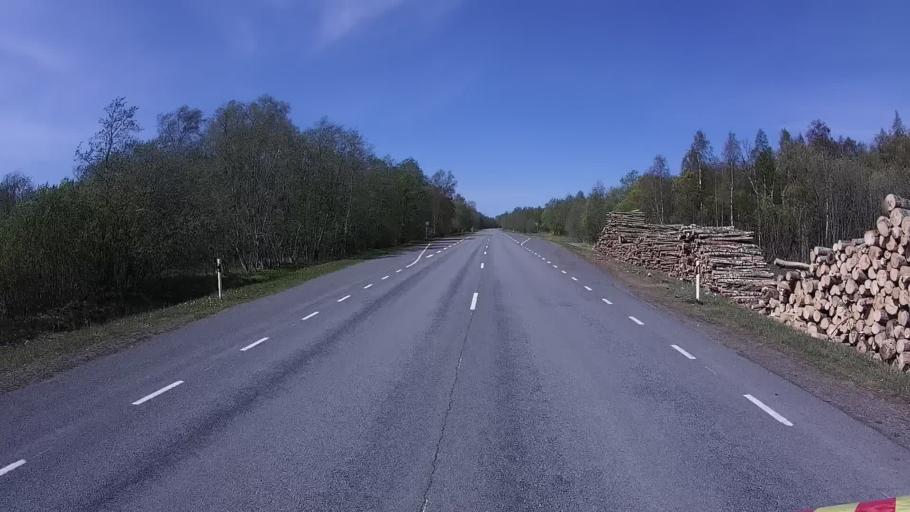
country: EE
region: Laeaene
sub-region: Lihula vald
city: Lihula
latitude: 58.8213
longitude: 23.7634
